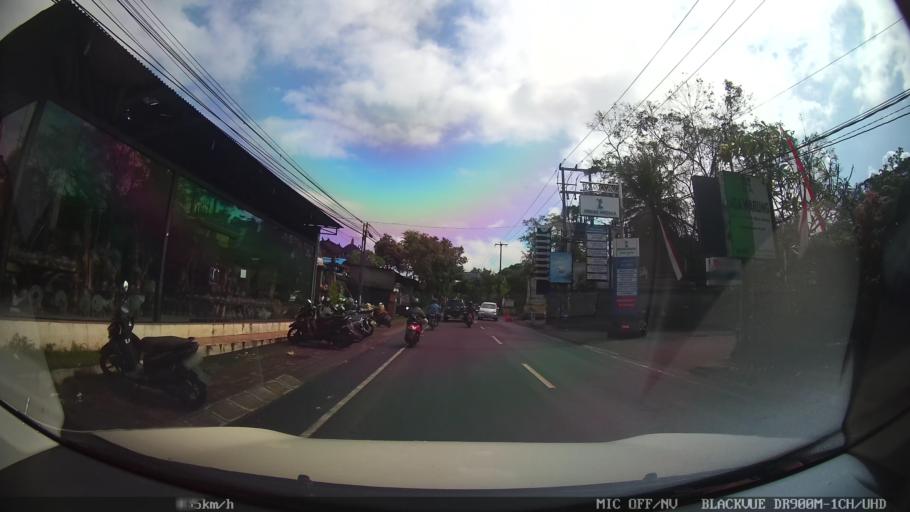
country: ID
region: Bali
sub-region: Kabupaten Gianyar
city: Ubud
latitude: -8.5335
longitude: 115.2721
